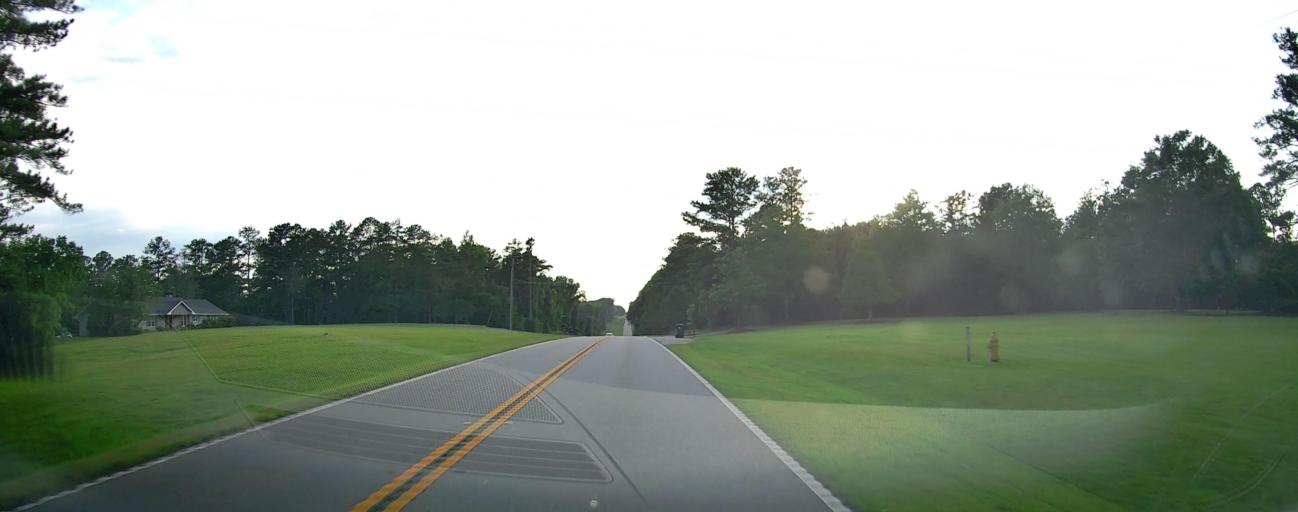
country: US
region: Georgia
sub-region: Peach County
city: Fort Valley
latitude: 32.5584
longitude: -83.9226
